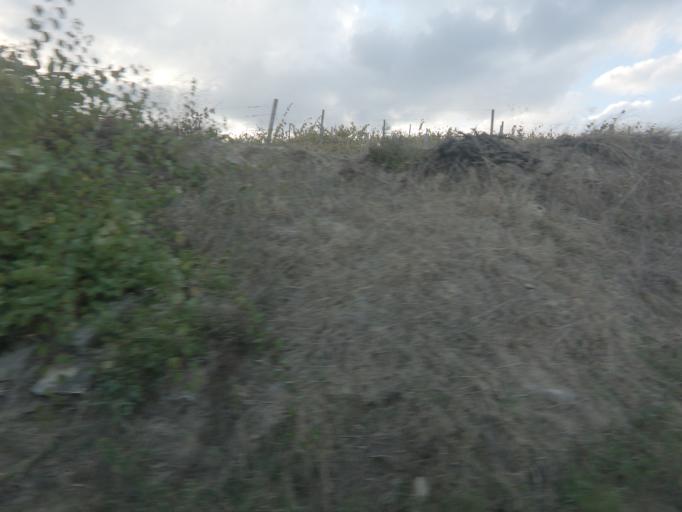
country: PT
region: Vila Real
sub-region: Mesao Frio
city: Mesao Frio
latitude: 41.1639
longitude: -7.8502
